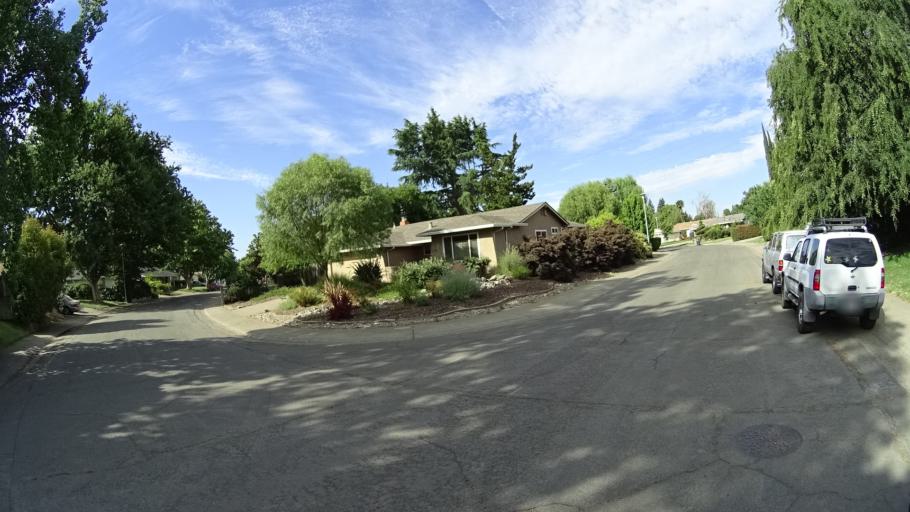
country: US
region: California
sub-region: Sacramento County
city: Rosemont
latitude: 38.5629
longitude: -121.3898
